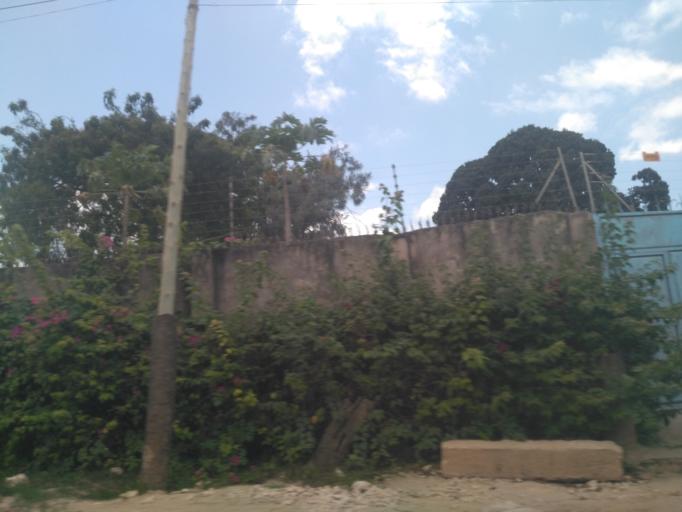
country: TZ
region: Dar es Salaam
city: Dar es Salaam
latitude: -6.8572
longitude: 39.2873
